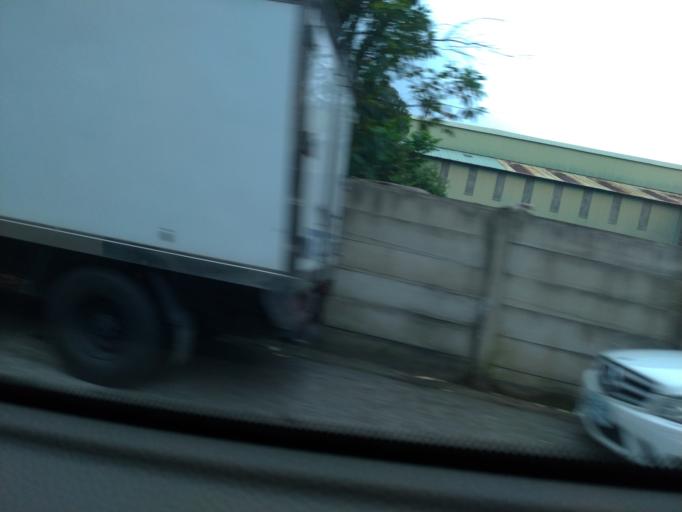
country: TW
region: Taipei
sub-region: Taipei
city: Banqiao
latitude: 24.9291
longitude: 121.4118
